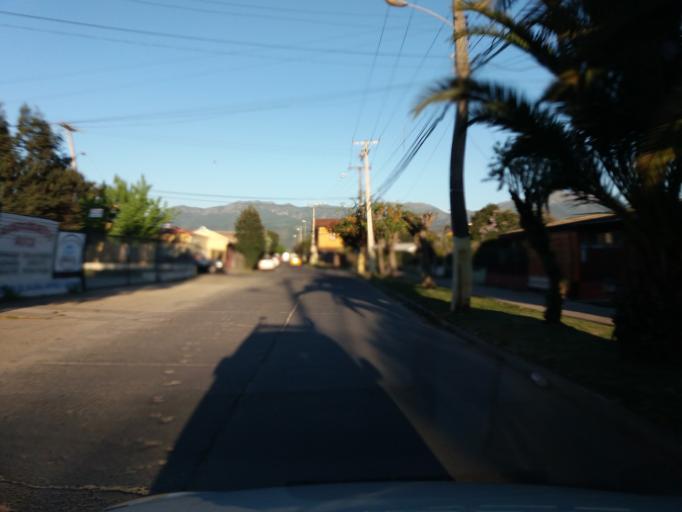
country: CL
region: Valparaiso
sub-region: Provincia de Quillota
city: Quillota
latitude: -32.8813
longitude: -71.2556
